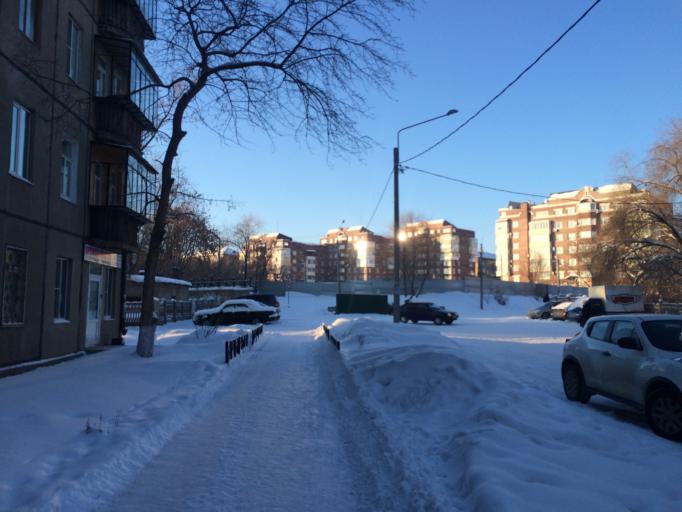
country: RU
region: Chelyabinsk
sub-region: Gorod Magnitogorsk
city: Magnitogorsk
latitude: 53.4148
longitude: 58.9895
